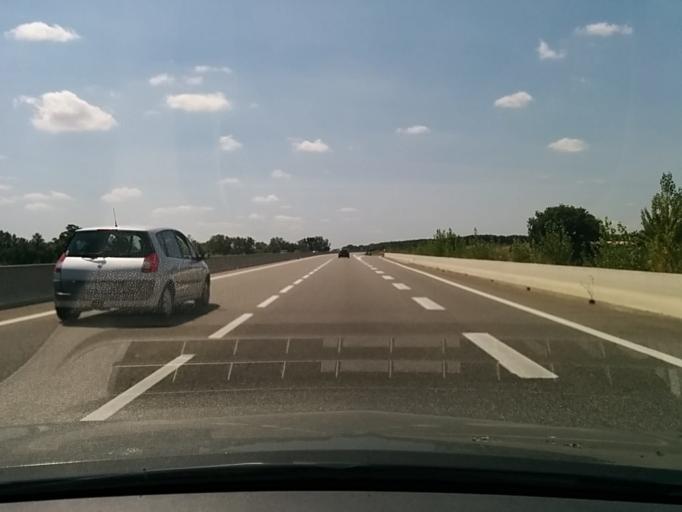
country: FR
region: Midi-Pyrenees
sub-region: Departement de la Haute-Garonne
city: La Salvetat-Saint-Gilles
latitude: 43.5897
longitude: 1.2729
